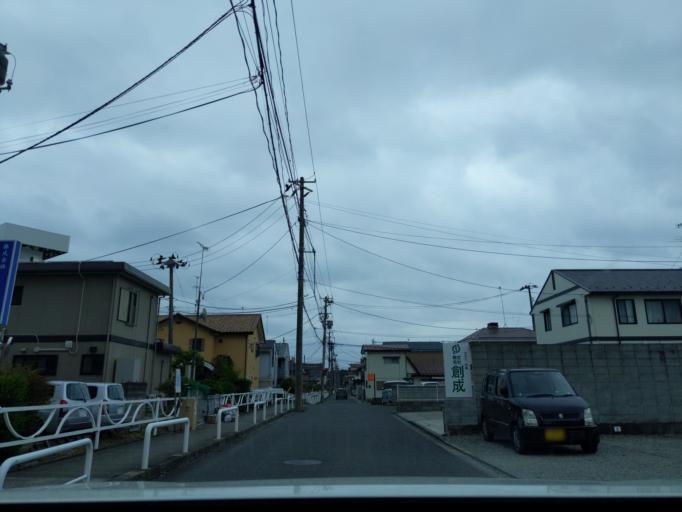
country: JP
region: Fukushima
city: Koriyama
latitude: 37.4049
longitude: 140.3508
